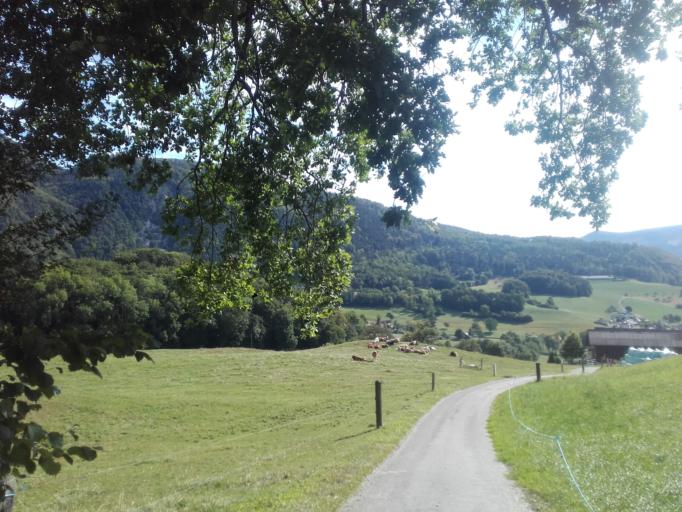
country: CH
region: Solothurn
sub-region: Bezirk Thal
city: Laupersdorf
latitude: 47.3178
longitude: 7.6384
